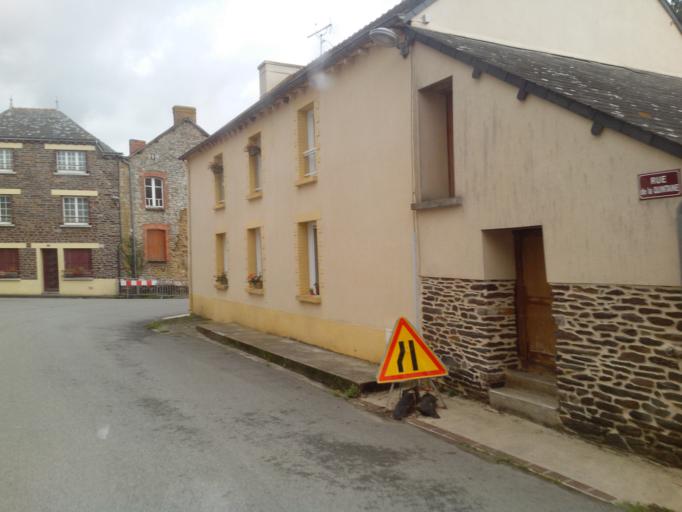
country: FR
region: Brittany
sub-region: Departement du Morbihan
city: Guilliers
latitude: 48.0888
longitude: -2.3634
